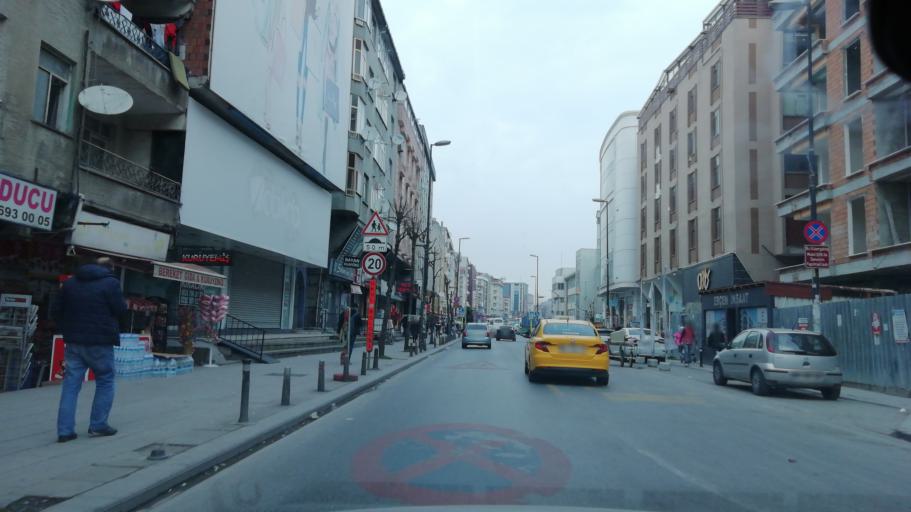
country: TR
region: Istanbul
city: Bahcelievler
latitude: 41.0102
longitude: 28.8414
